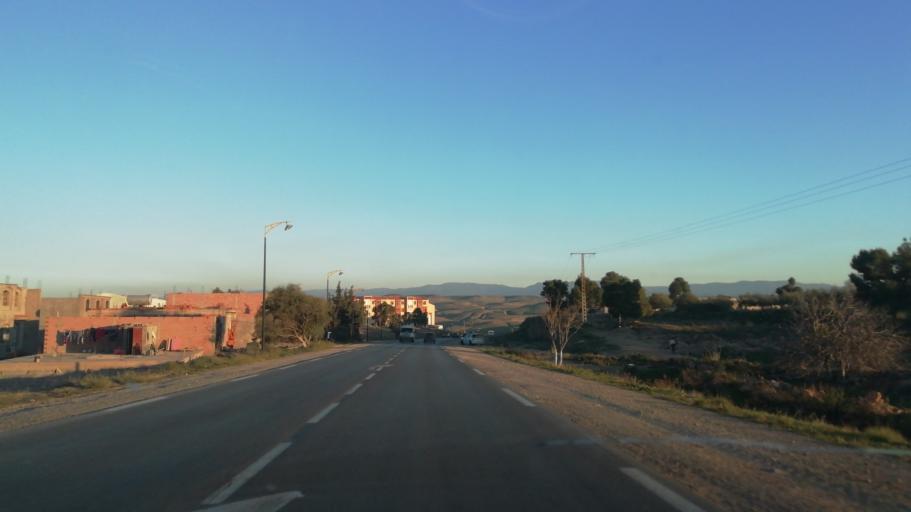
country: DZ
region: Tlemcen
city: Nedroma
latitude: 34.8908
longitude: -1.6558
